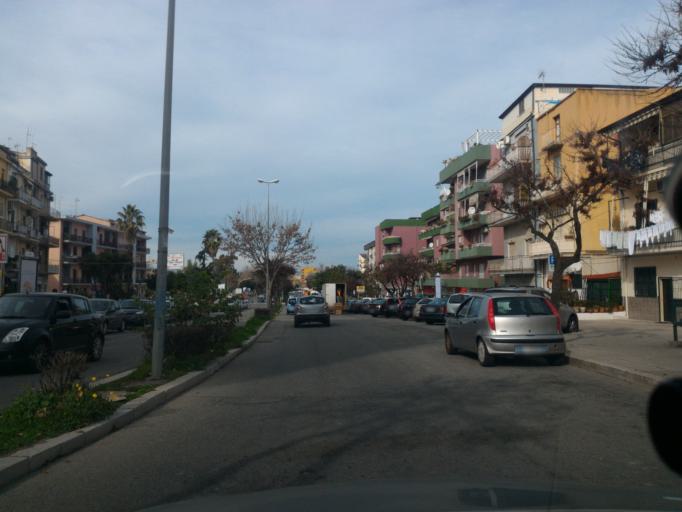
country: IT
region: Calabria
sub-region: Provincia di Crotone
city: Crotone
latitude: 39.0779
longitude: 17.1250
